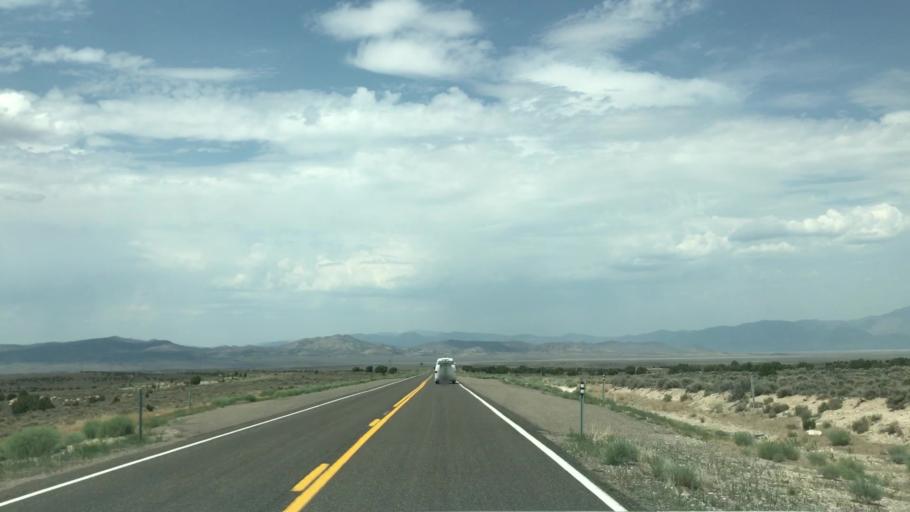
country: US
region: Nevada
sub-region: Eureka County
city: Eureka
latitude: 39.3933
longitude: -115.5186
